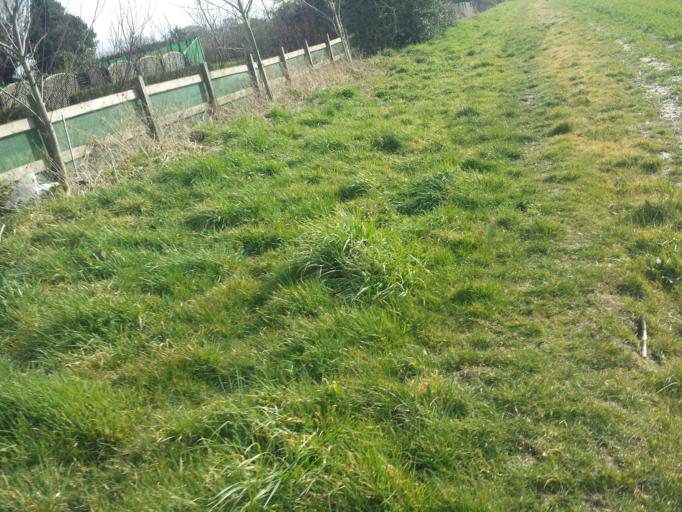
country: GB
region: England
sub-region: Essex
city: Little Clacton
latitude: 51.8856
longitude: 1.1601
